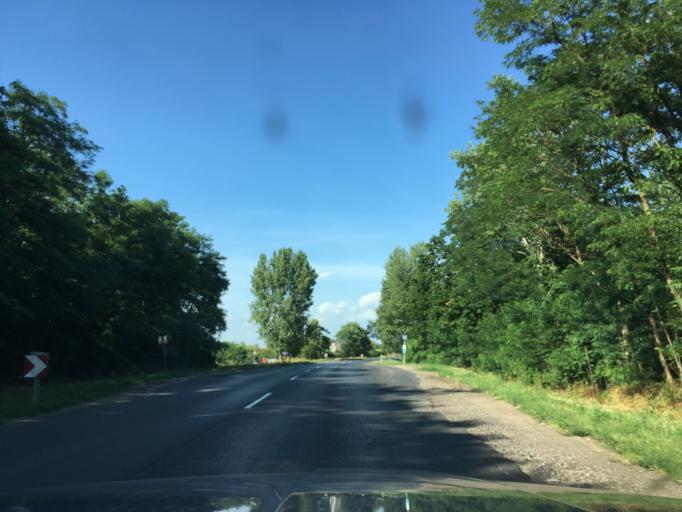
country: HU
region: Hajdu-Bihar
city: Debrecen
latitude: 47.5616
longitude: 21.6748
